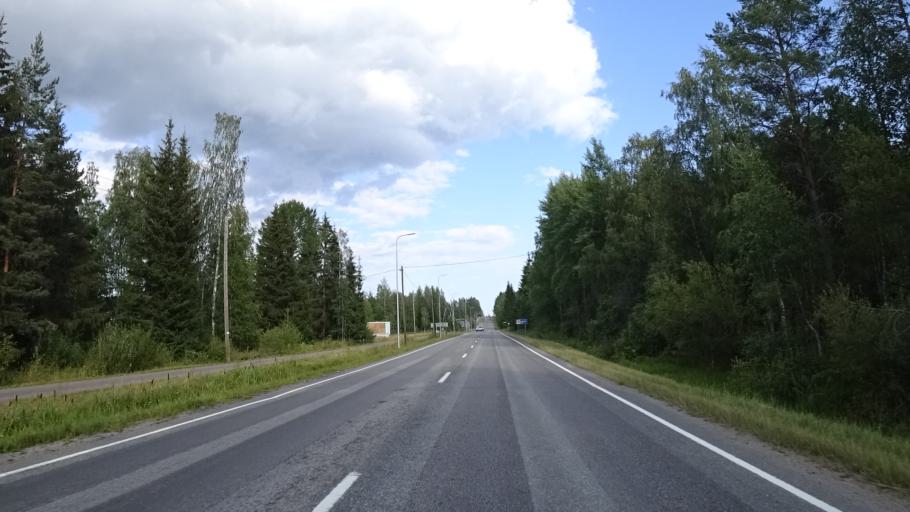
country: FI
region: South Karelia
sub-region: Imatra
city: Imatra
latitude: 61.1732
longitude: 28.7297
